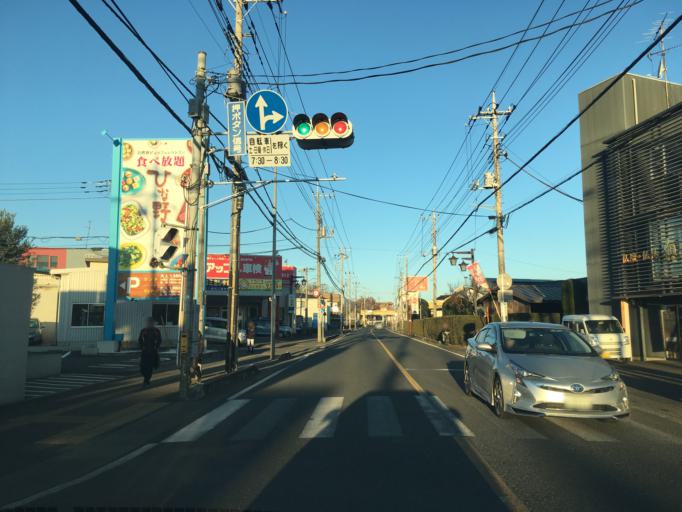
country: JP
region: Saitama
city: Sayama
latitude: 35.8129
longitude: 139.4262
